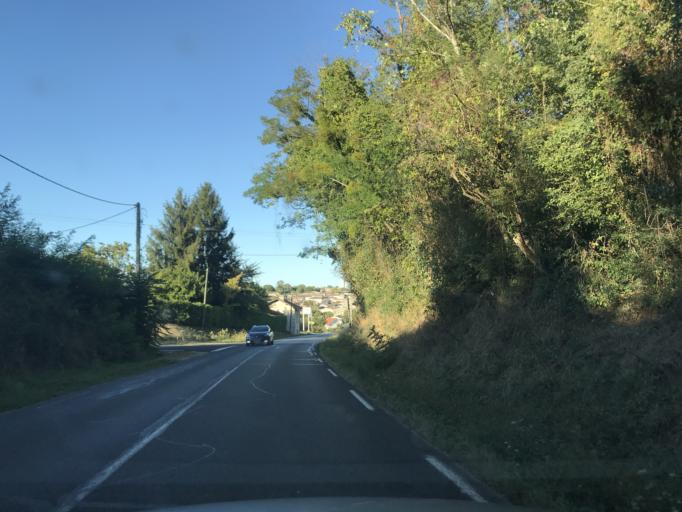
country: FR
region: Aquitaine
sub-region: Departement de la Gironde
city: Sauveterre-de-Guyenne
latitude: 44.6878
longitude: -0.0912
